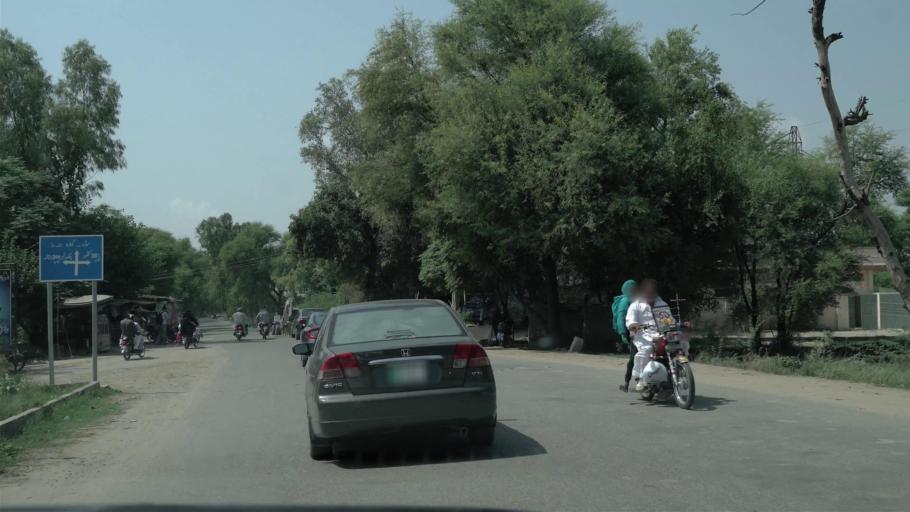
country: PK
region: Punjab
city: Gojra
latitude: 31.1696
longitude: 72.6232
